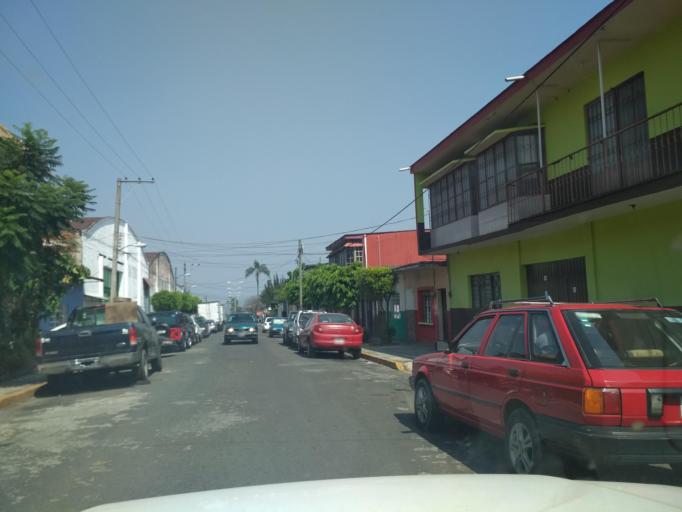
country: MX
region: Veracruz
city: Orizaba
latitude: 18.8412
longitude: -97.0959
